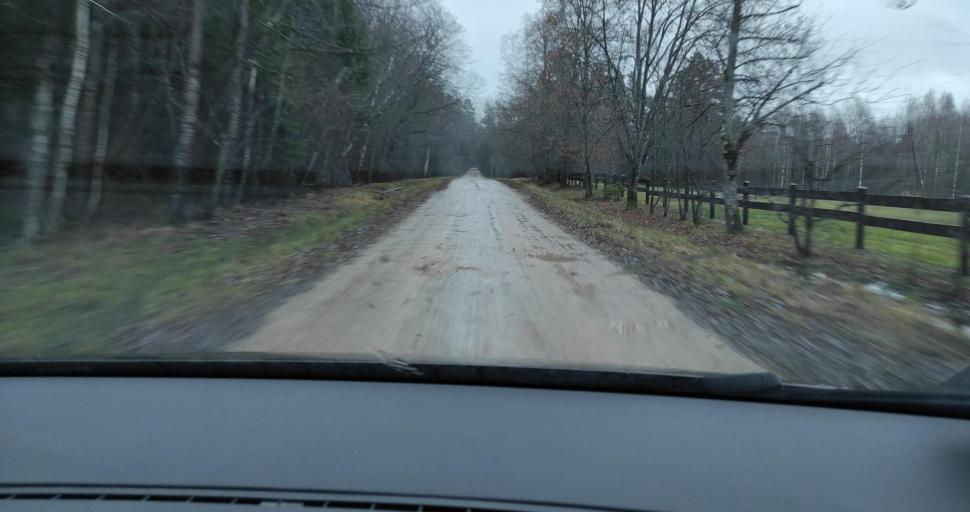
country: LV
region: Skrunda
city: Skrunda
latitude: 56.6077
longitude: 22.1509
